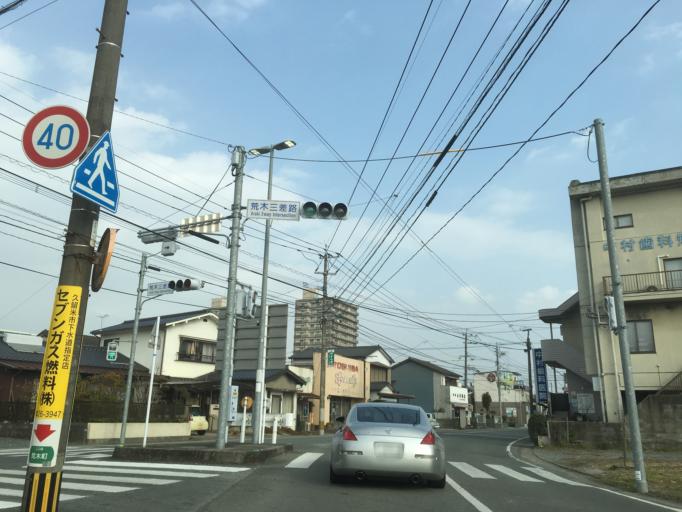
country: JP
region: Fukuoka
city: Kurume
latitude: 33.2761
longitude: 130.5002
